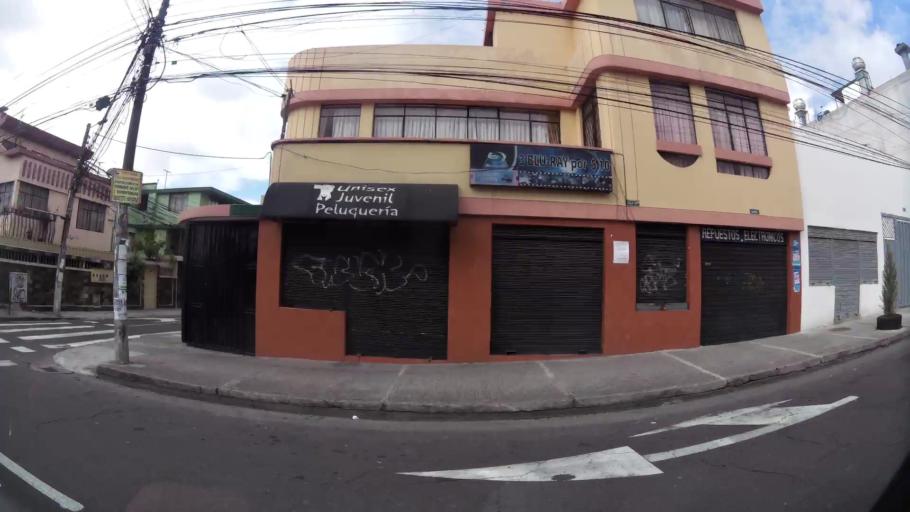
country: EC
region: Pichincha
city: Quito
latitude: -0.1431
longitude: -78.4939
